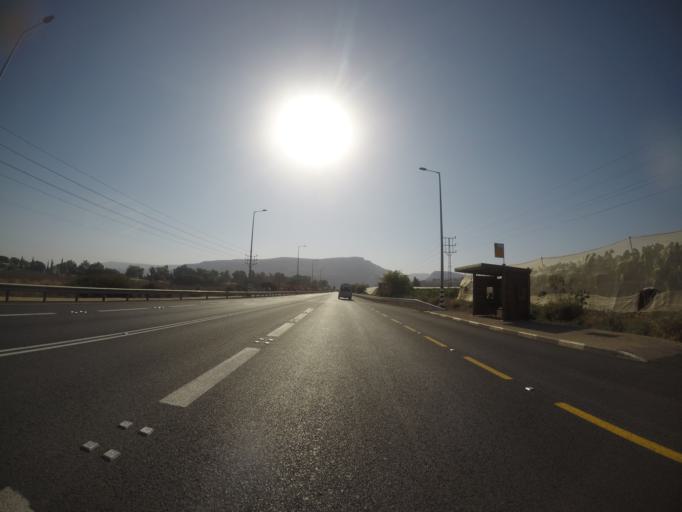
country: IL
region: Northern District
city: Tiberias
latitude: 32.8486
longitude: 35.5186
